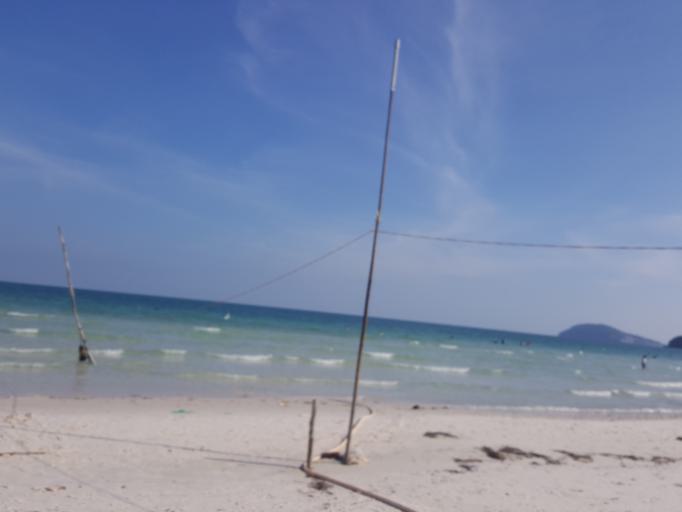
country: VN
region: Kien Giang
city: Duong GJong
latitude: 10.0571
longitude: 104.0363
